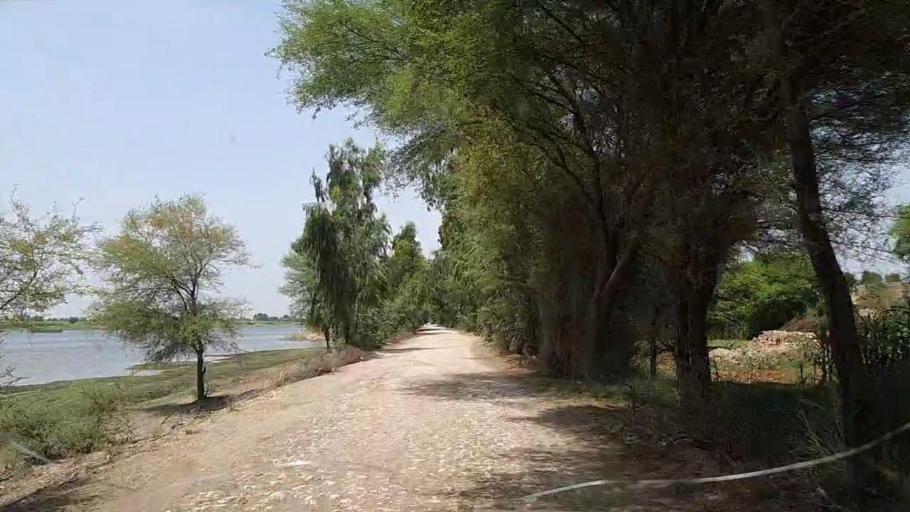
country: PK
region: Sindh
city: Ghotki
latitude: 28.0838
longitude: 69.3115
